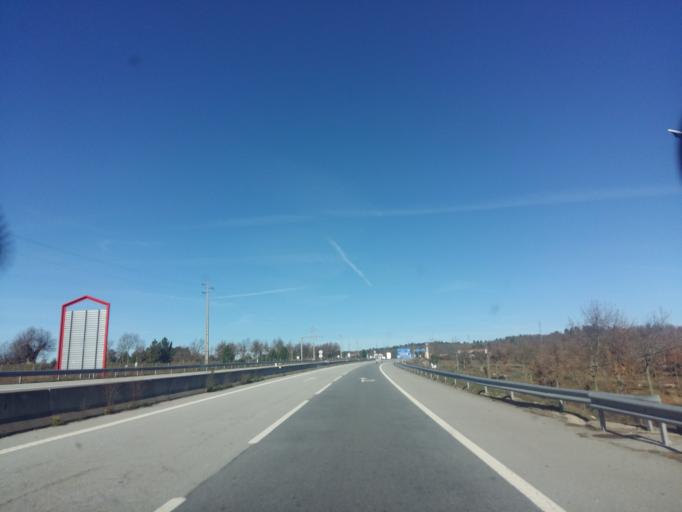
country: PT
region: Guarda
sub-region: Guarda
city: Sequeira
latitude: 40.5386
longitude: -7.2173
